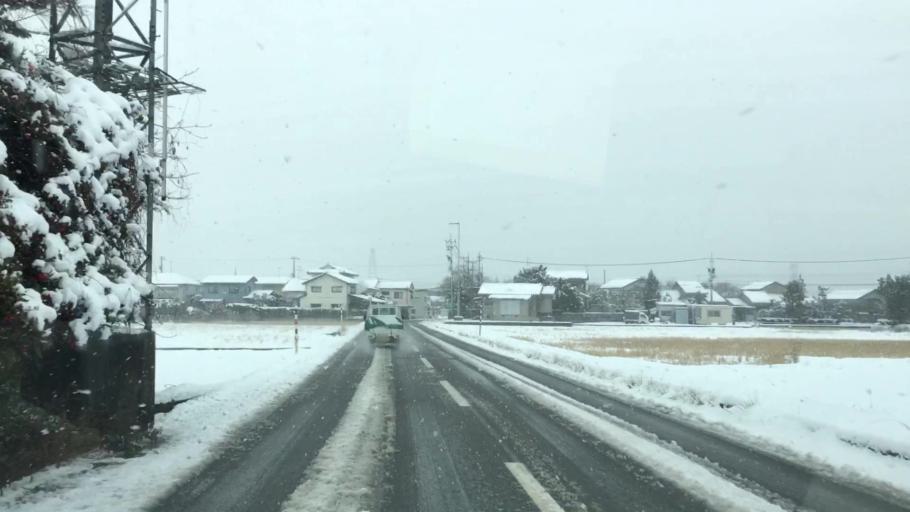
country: JP
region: Toyama
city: Kamiichi
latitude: 36.6993
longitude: 137.3360
